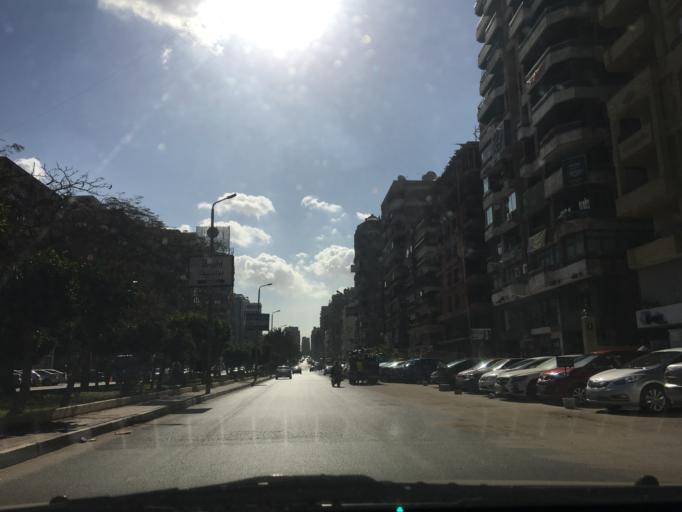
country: EG
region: Muhafazat al Qahirah
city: Cairo
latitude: 30.0567
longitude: 31.3458
